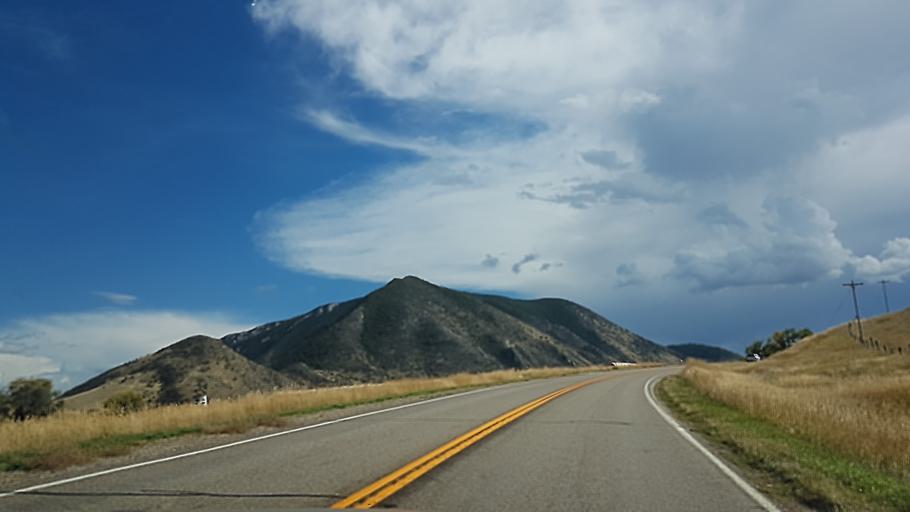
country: US
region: Montana
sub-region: Jefferson County
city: Whitehall
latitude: 45.8339
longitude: -111.9356
